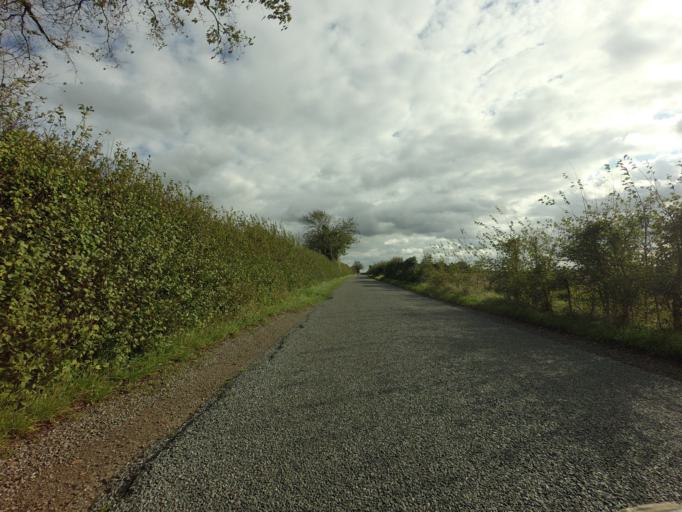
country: GB
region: England
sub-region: Norfolk
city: Dersingham
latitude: 52.8584
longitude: 0.5146
